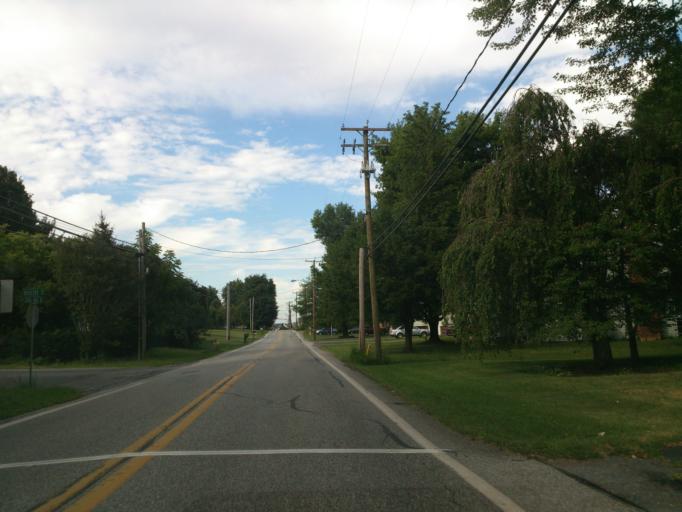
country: US
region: Pennsylvania
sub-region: Lebanon County
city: Campbelltown
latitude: 40.2729
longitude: -76.5893
